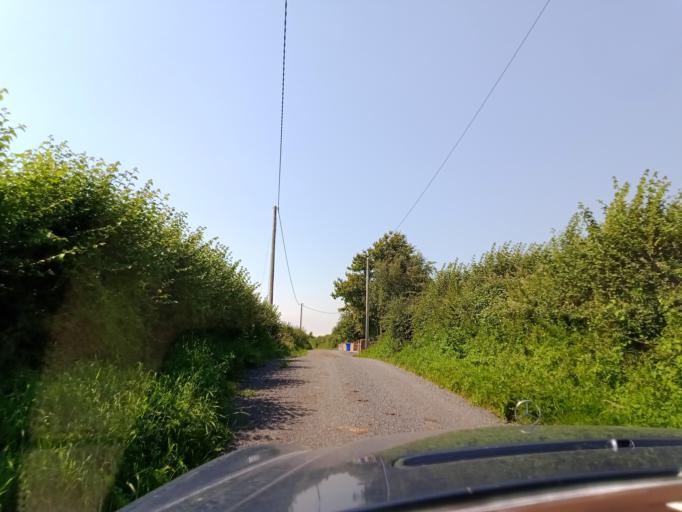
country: IE
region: Leinster
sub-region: Kilkenny
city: Mooncoin
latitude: 52.3121
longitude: -7.2787
